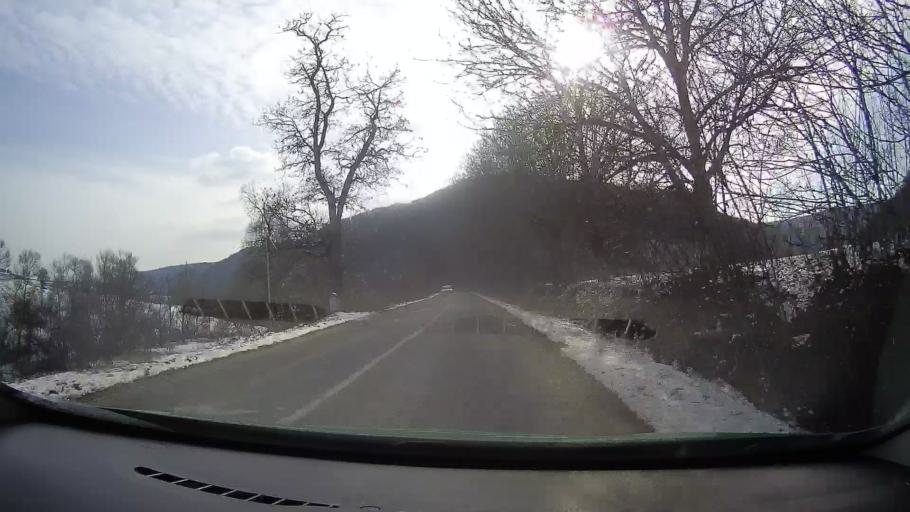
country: RO
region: Mures
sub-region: Comuna Apold
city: Saes
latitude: 46.1691
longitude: 24.7579
